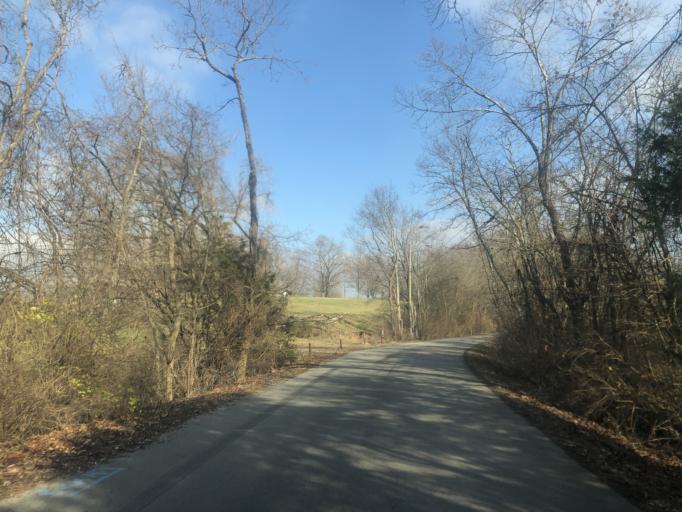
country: US
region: Tennessee
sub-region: Rutherford County
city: La Vergne
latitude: 36.0596
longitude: -86.6573
